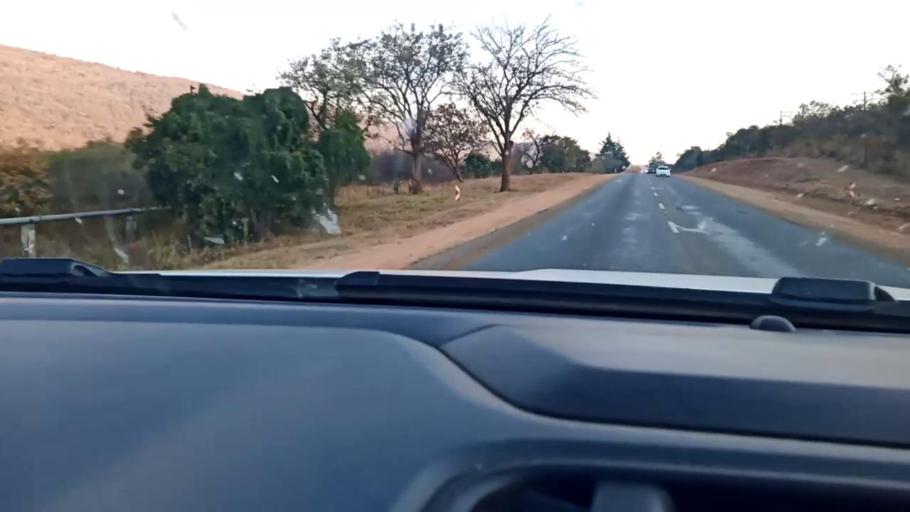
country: ZA
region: Limpopo
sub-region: Mopani District Municipality
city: Duiwelskloof
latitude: -23.6566
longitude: 30.1694
